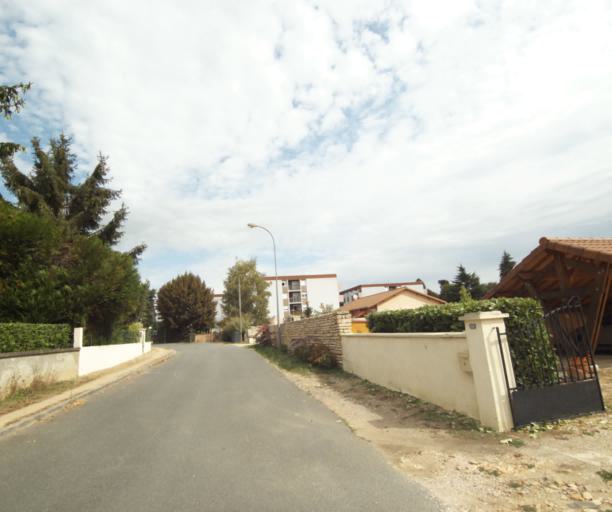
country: FR
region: Bourgogne
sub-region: Departement de Saone-et-Loire
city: Tournus
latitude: 46.5583
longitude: 4.9049
